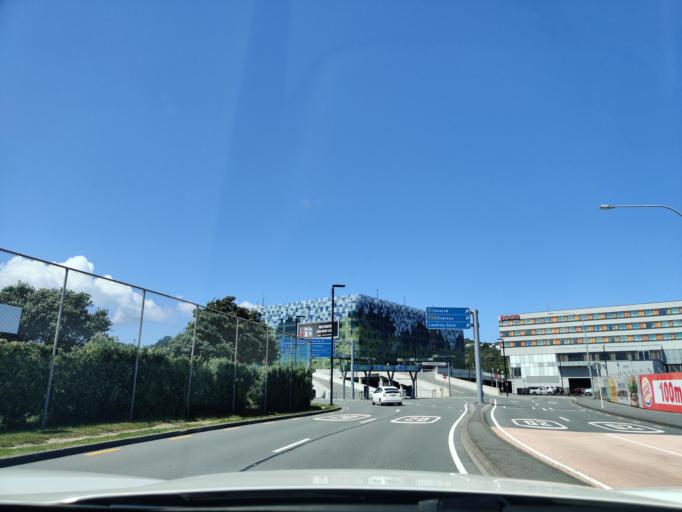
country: NZ
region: Wellington
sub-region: Wellington City
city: Wellington
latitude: -41.3266
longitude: 174.8114
